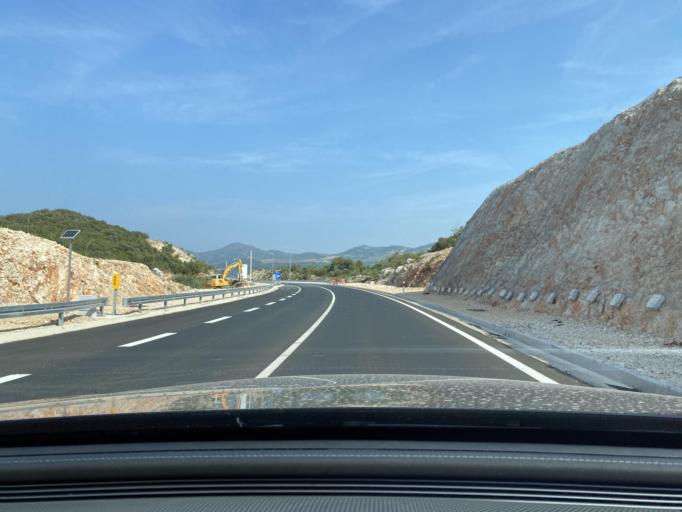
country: BA
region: Federation of Bosnia and Herzegovina
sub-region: Hercegovacko-Bosanski Kanton
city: Neum
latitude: 42.9160
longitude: 17.5282
